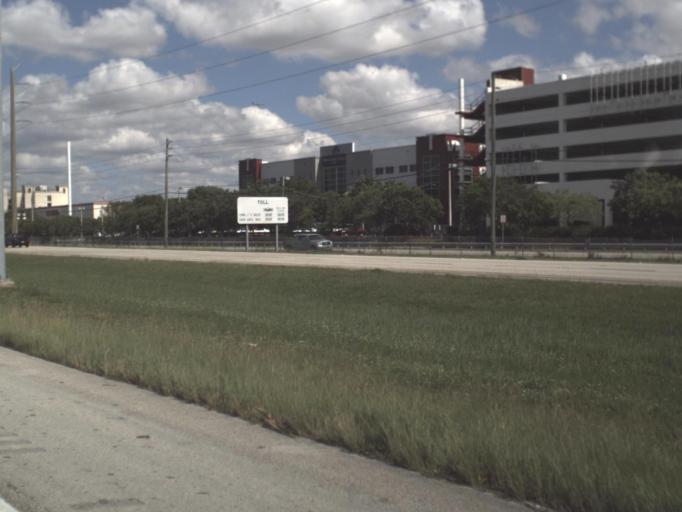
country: US
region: Florida
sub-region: Miami-Dade County
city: Doral
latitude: 25.8072
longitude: -80.3861
